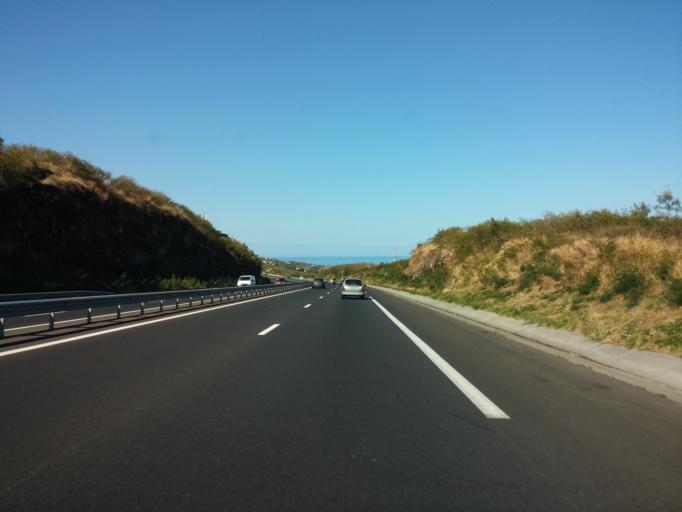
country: RE
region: Reunion
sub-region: Reunion
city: Saint-Leu
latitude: -21.1781
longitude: 55.2968
